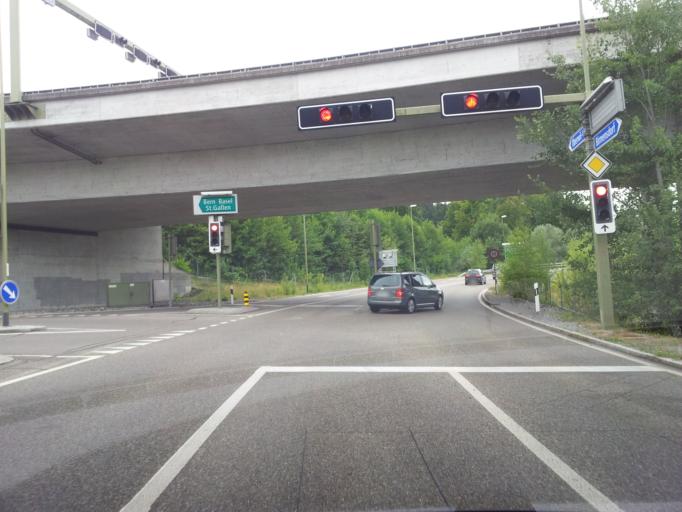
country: CH
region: Zurich
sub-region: Bezirk Dietikon
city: Birmensdorf
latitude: 47.3479
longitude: 8.4275
